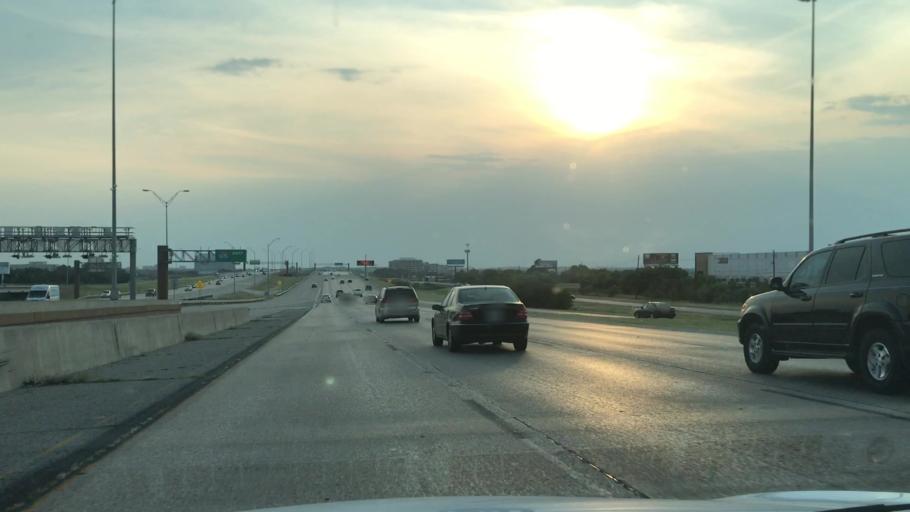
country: US
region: Texas
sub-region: Dallas County
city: Farmers Branch
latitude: 32.9086
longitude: -96.9014
